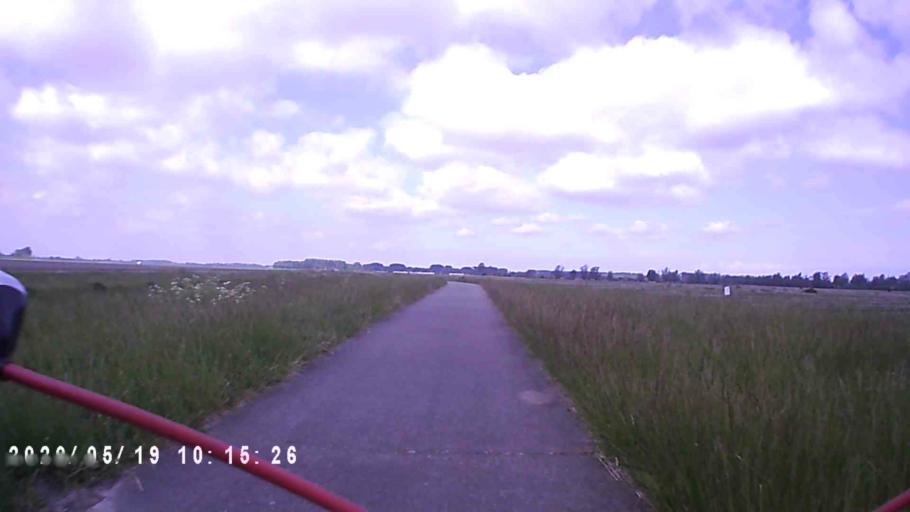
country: NL
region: Friesland
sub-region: Gemeente Kollumerland en Nieuwkruisland
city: Kollum
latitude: 53.3214
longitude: 6.2151
